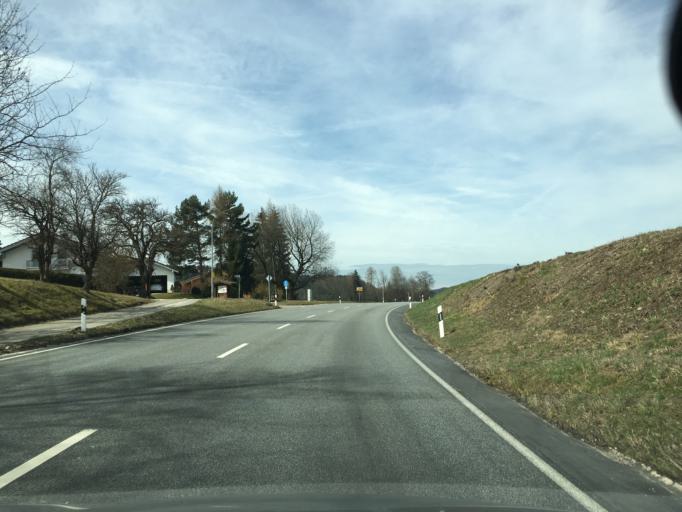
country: DE
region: Bavaria
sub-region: Upper Bavaria
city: Siegsdorf
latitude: 47.8026
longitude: 12.6977
